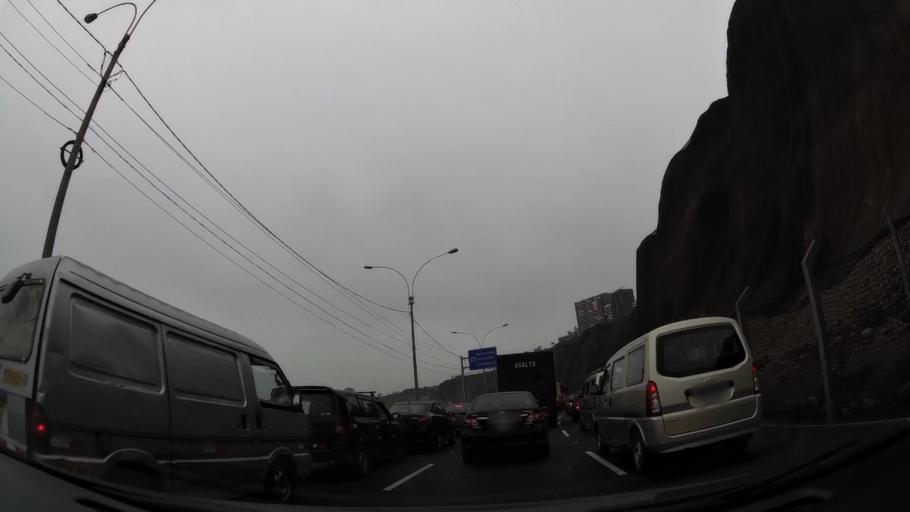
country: PE
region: Lima
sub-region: Lima
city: San Isidro
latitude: -12.1163
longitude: -77.0498
